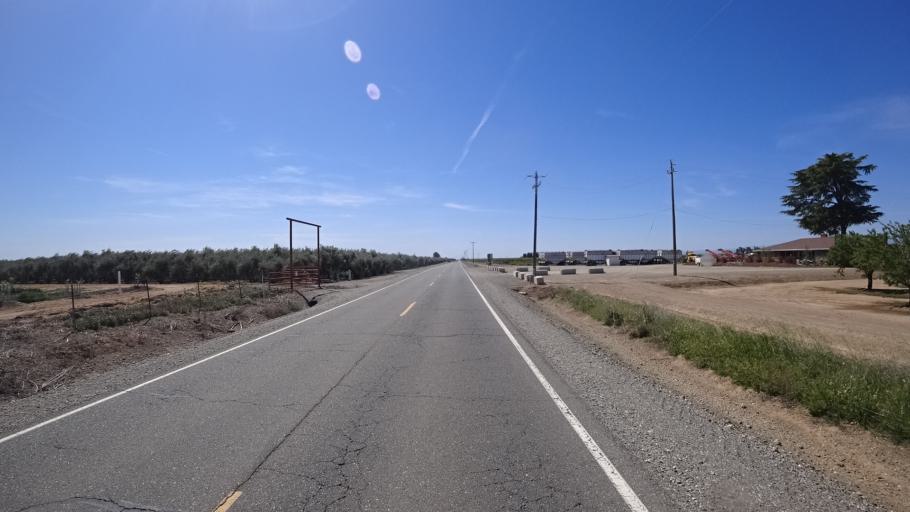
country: US
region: California
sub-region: Glenn County
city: Orland
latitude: 39.6892
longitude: -122.1402
